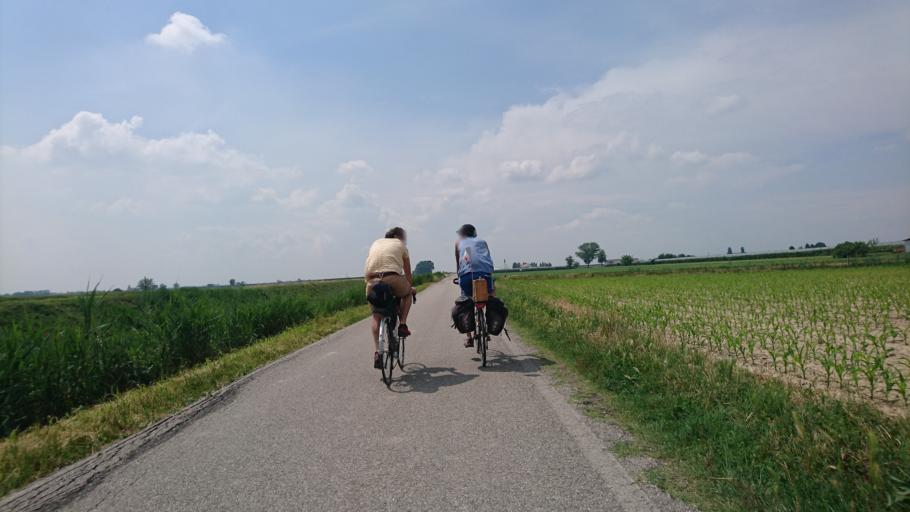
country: IT
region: Veneto
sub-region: Provincia di Rovigo
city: Giacciano con Baruchella
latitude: 45.0695
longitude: 11.4391
